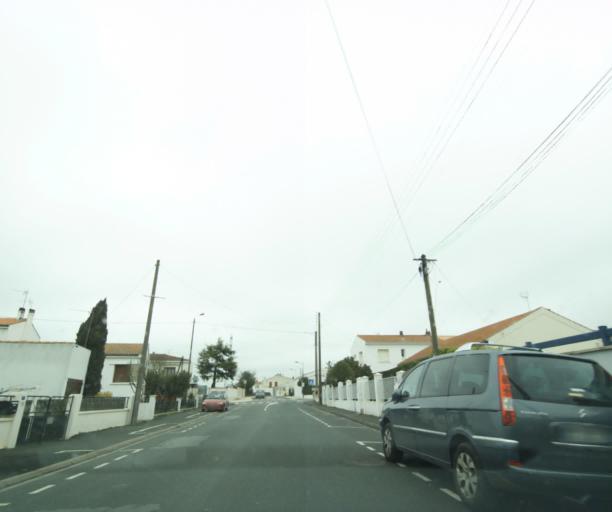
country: FR
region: Poitou-Charentes
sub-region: Departement de la Charente-Maritime
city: Lagord
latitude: 46.1793
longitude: -1.1406
